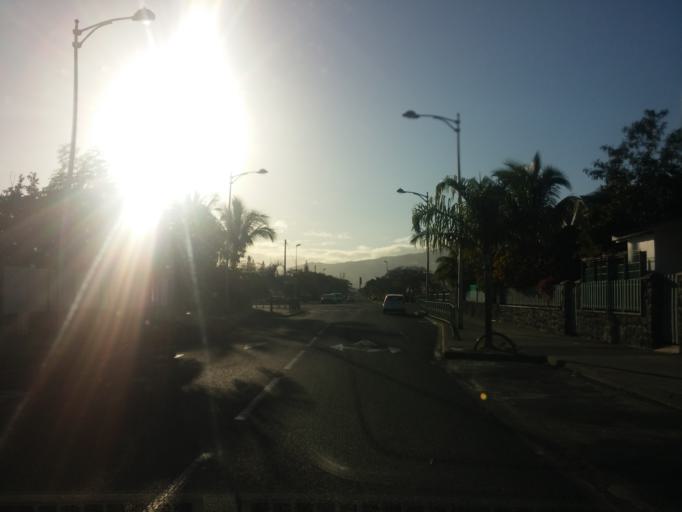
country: RE
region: Reunion
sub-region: Reunion
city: Le Port
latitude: -20.9353
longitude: 55.2983
